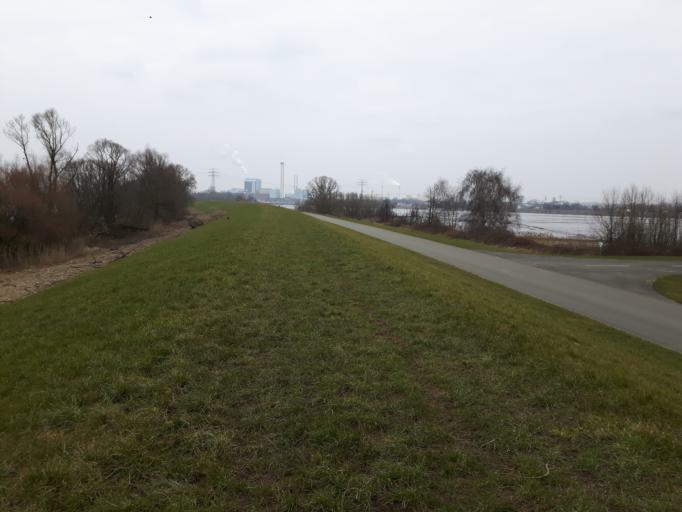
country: DE
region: Hamburg
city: Rothenburgsort
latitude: 53.5107
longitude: 10.0623
